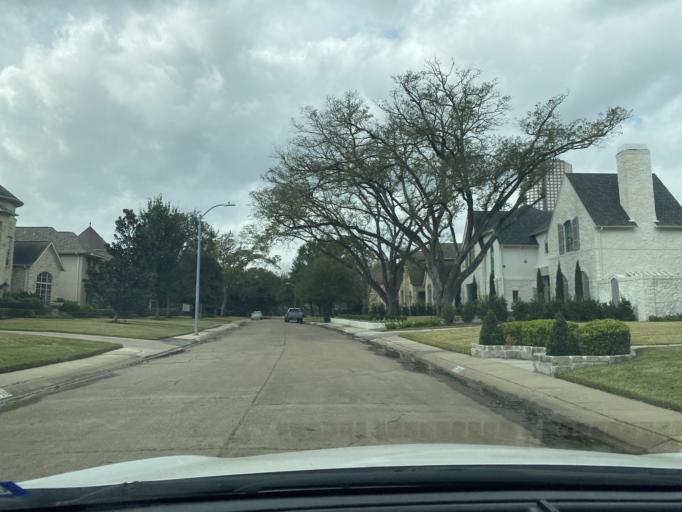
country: US
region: Texas
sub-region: Harris County
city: Hunters Creek Village
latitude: 29.7470
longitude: -95.4754
